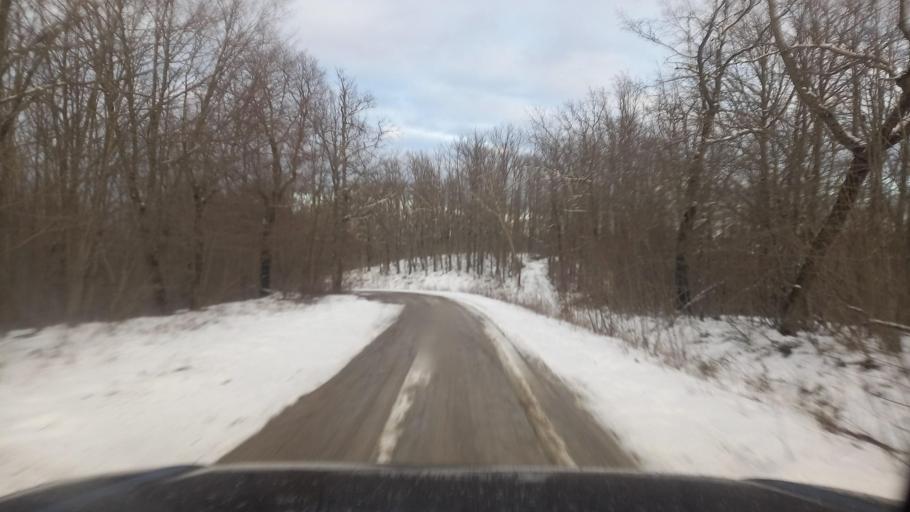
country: RU
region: Krasnodarskiy
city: Smolenskaya
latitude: 44.6781
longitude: 38.7742
